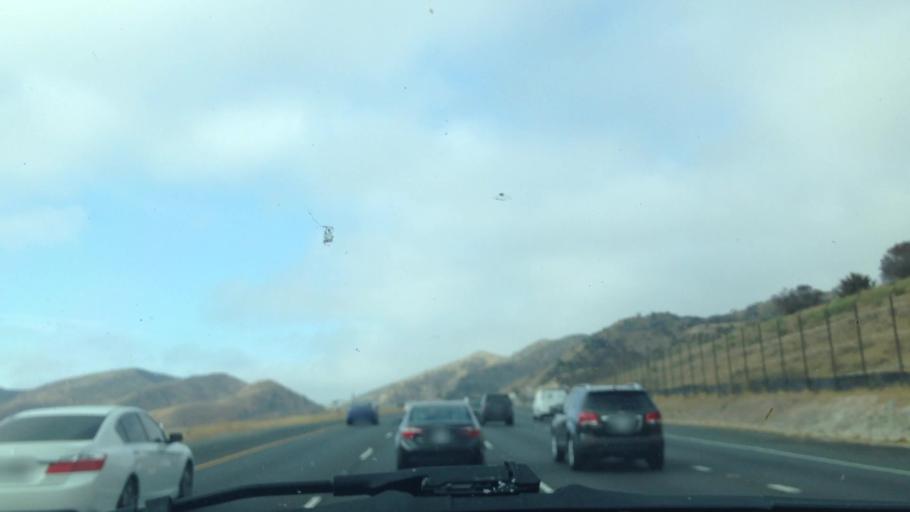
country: US
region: California
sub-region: Orange County
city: Villa Park
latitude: 33.8461
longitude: -117.7173
